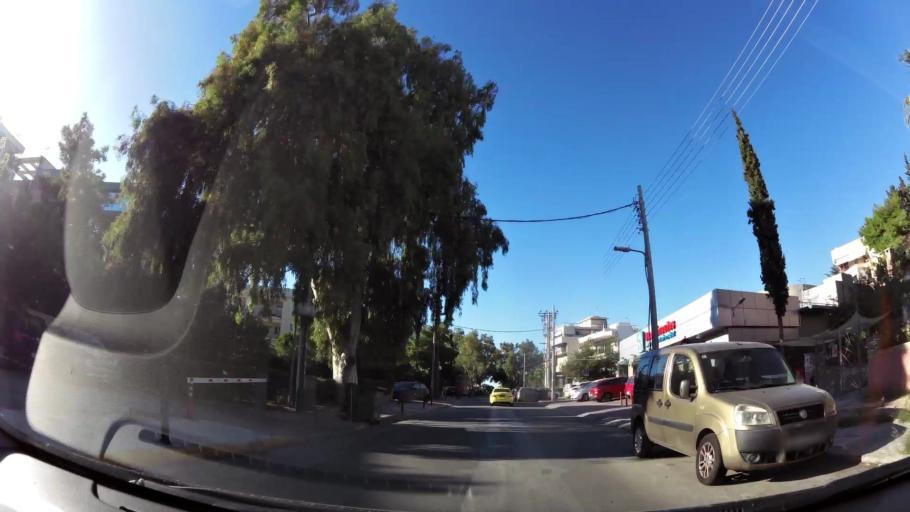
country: GR
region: Attica
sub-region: Nomarchia Anatolikis Attikis
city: Voula
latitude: 37.8380
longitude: 23.7693
